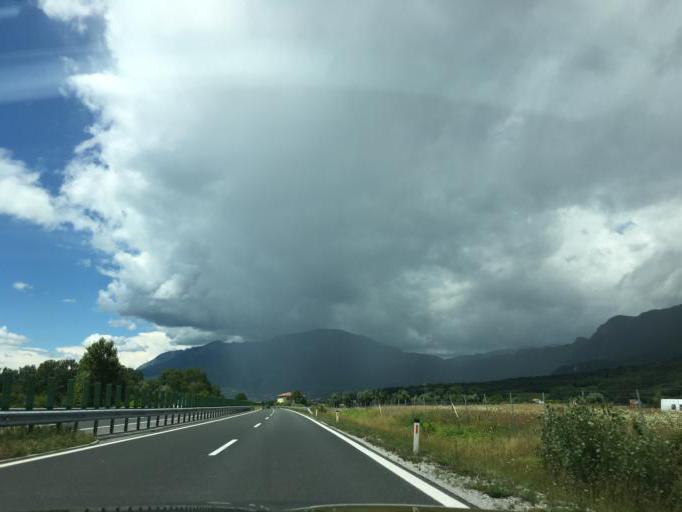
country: SI
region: Ajdovscina
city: Ajdovscina
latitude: 45.8681
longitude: 13.9308
